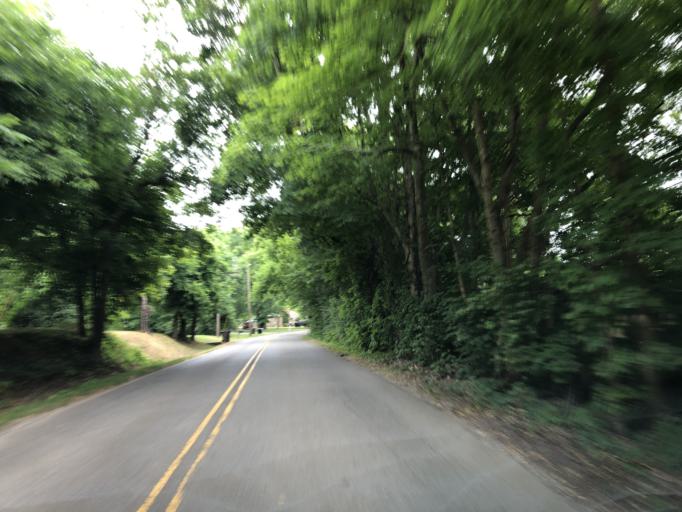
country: US
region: Tennessee
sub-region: Davidson County
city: Goodlettsville
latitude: 36.2864
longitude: -86.7594
